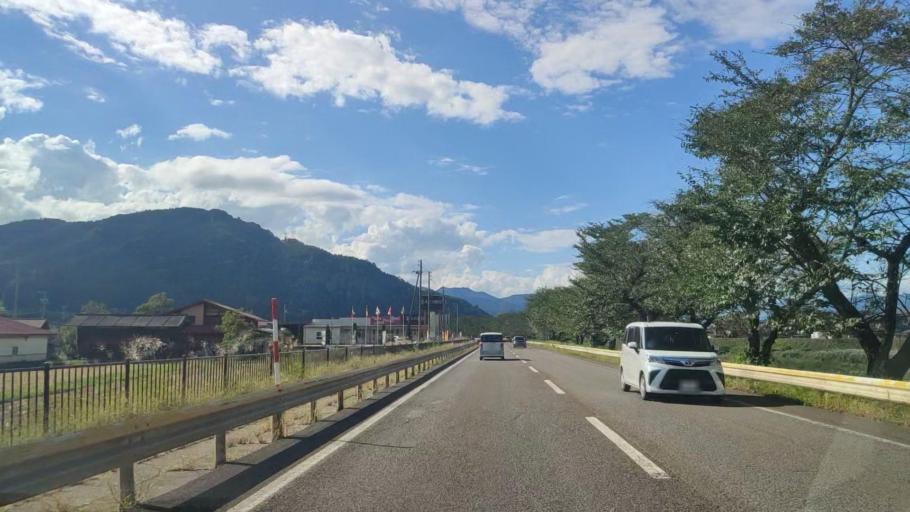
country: JP
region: Gifu
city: Takayama
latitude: 36.2077
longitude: 137.2172
